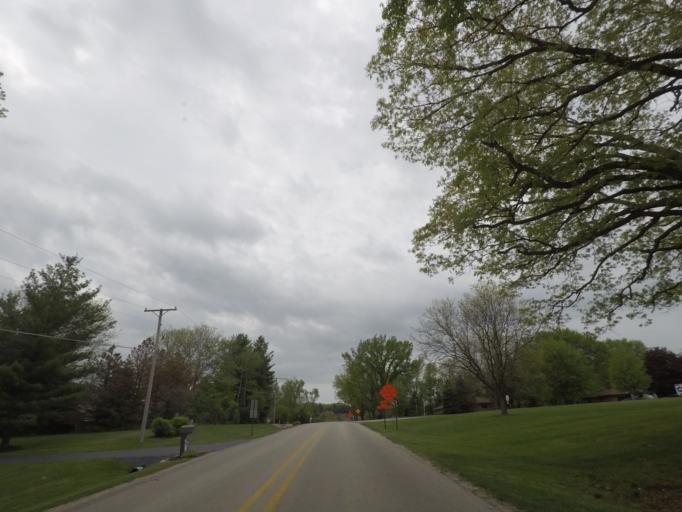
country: US
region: Illinois
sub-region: Winnebago County
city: Roscoe
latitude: 42.4299
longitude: -88.9782
